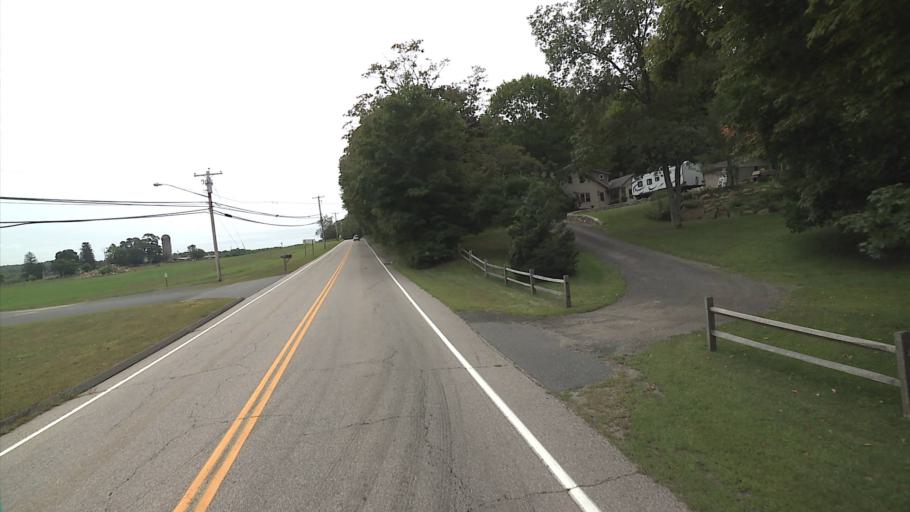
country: US
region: Connecticut
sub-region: Middlesex County
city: Essex Village
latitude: 41.3810
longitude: -72.3500
